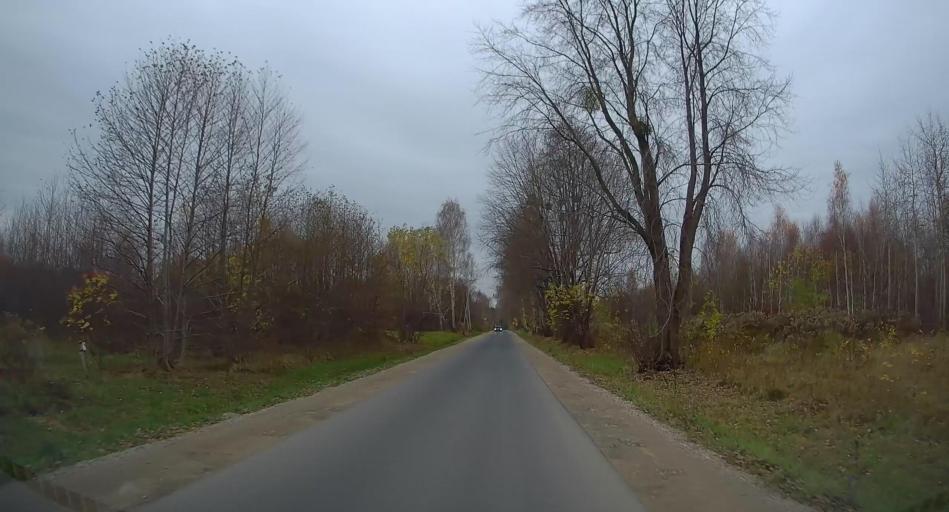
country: PL
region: Lodz Voivodeship
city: Zabia Wola
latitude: 52.0148
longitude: 20.6555
